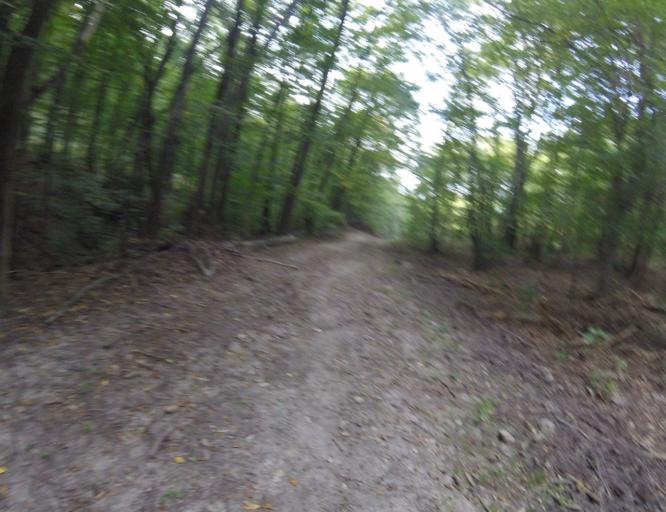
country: HU
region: Pest
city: Nagykovacsi
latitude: 47.6799
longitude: 19.0126
